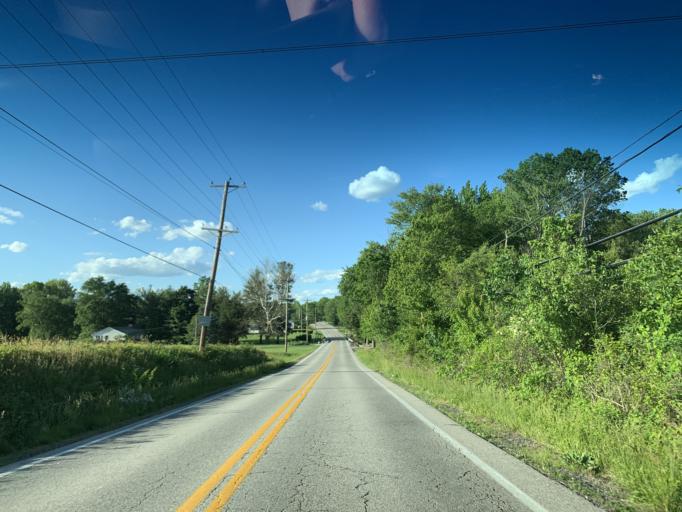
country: US
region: Maryland
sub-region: Cecil County
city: Elkton
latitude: 39.6375
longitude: -75.8140
